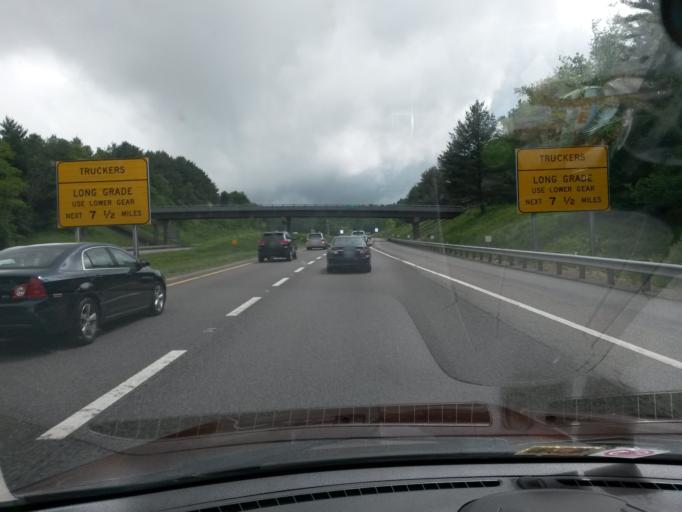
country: US
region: Virginia
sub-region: Carroll County
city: Cana
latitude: 36.6677
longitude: -80.7090
